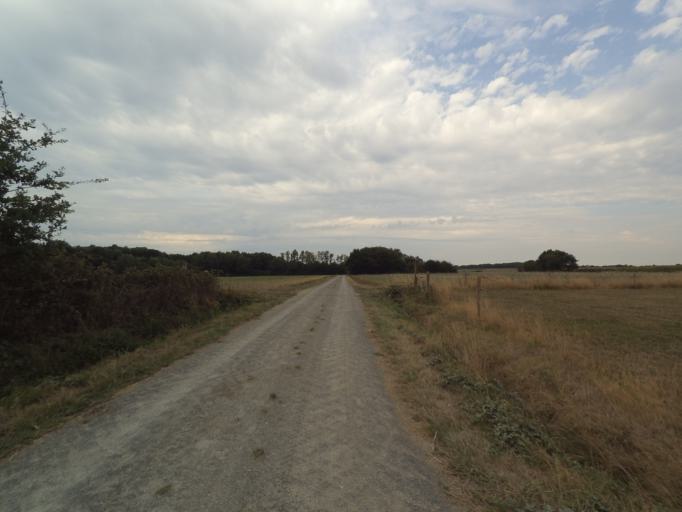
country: FR
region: Pays de la Loire
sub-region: Departement de la Loire-Atlantique
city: Vieillevigne
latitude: 46.9870
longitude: -1.3899
